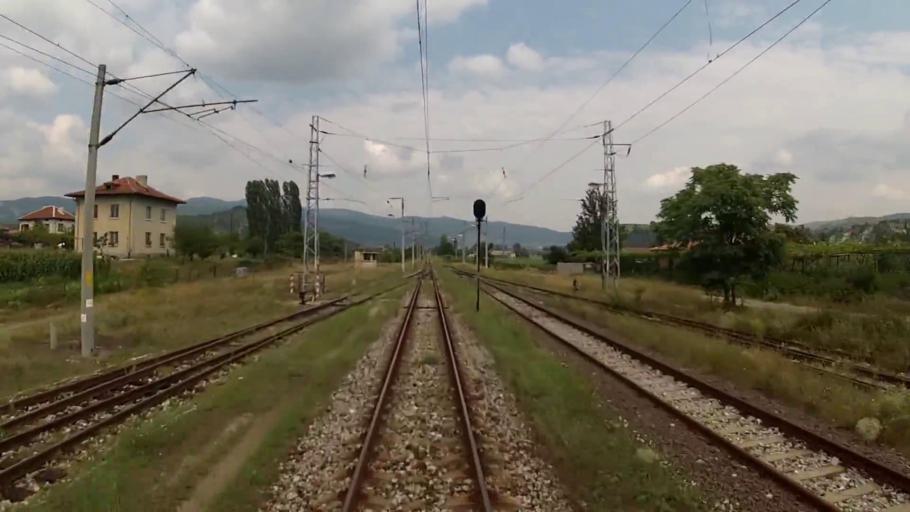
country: BG
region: Blagoevgrad
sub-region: Obshtina Simitli
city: Simitli
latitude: 41.8573
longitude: 23.1315
